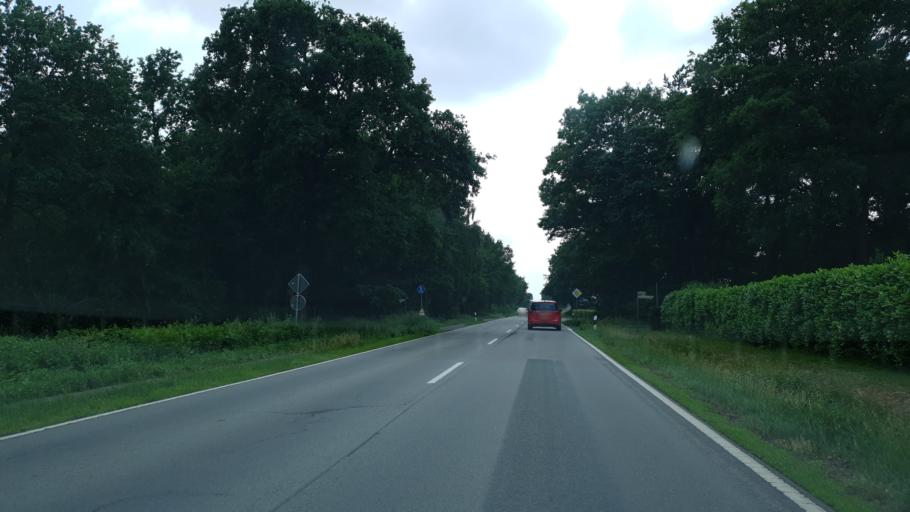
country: DE
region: Lower Saxony
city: Geeste
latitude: 52.5739
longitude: 7.2141
